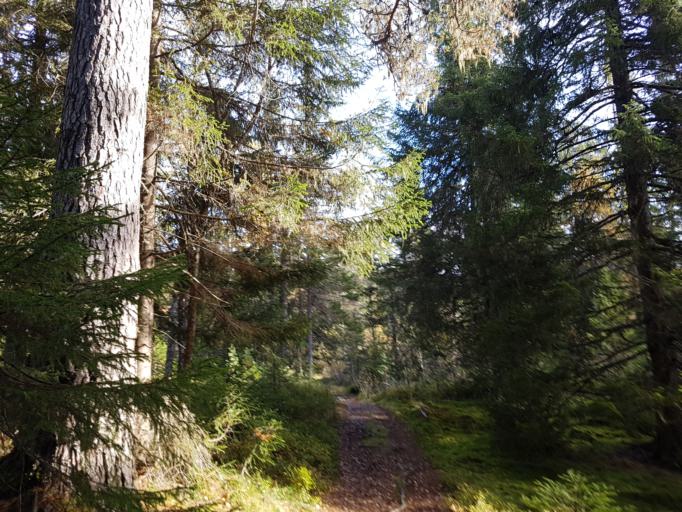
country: NO
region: Sor-Trondelag
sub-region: Trondheim
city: Trondheim
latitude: 63.4444
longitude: 10.2847
